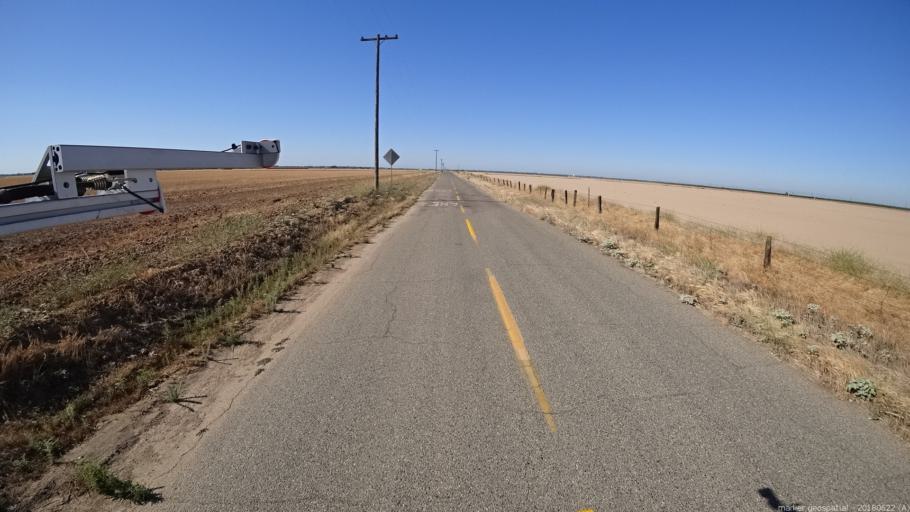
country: US
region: California
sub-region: Madera County
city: Bonadelle Ranchos-Madera Ranchos
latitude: 36.8938
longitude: -119.8109
